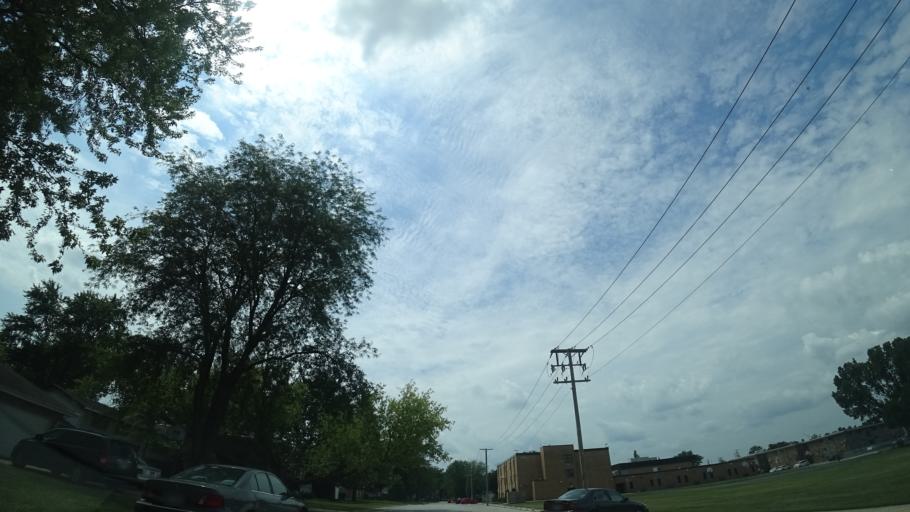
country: US
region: Illinois
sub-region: Cook County
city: Worth
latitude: 41.6883
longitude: -87.7894
